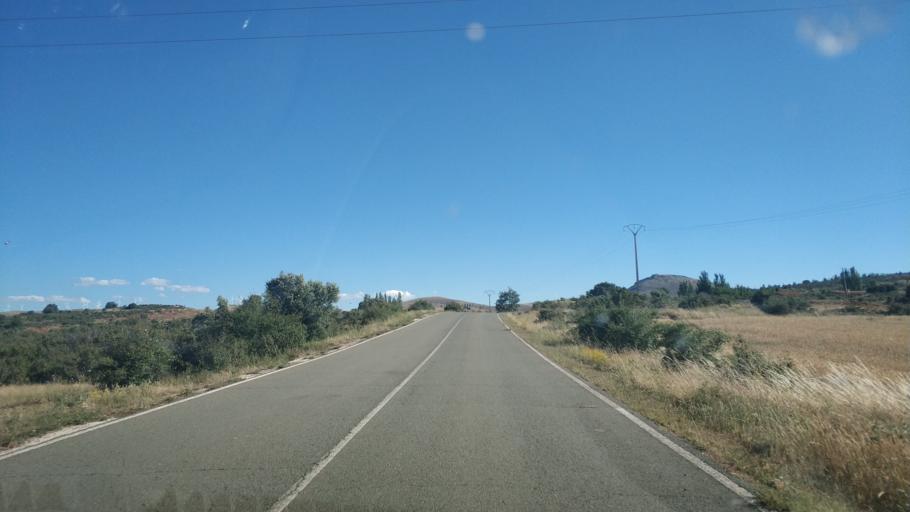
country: ES
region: Castille and Leon
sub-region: Provincia de Soria
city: Montejo de Tiermes
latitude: 41.3393
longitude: -3.1511
